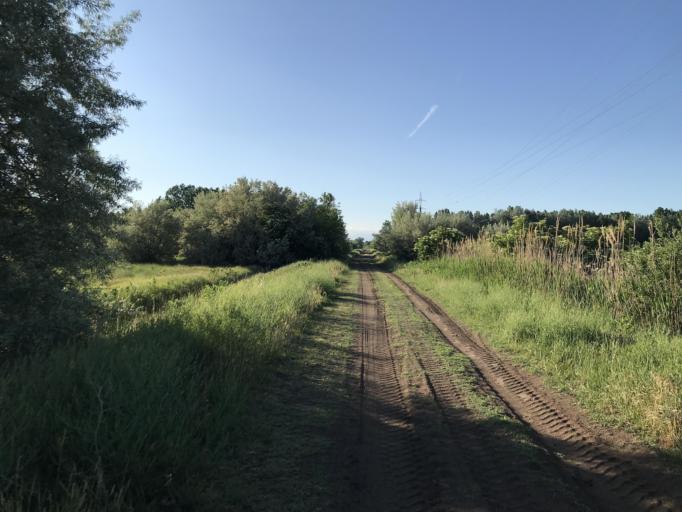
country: HU
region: Bacs-Kiskun
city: Tiszakecske
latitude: 46.9733
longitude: 20.0613
